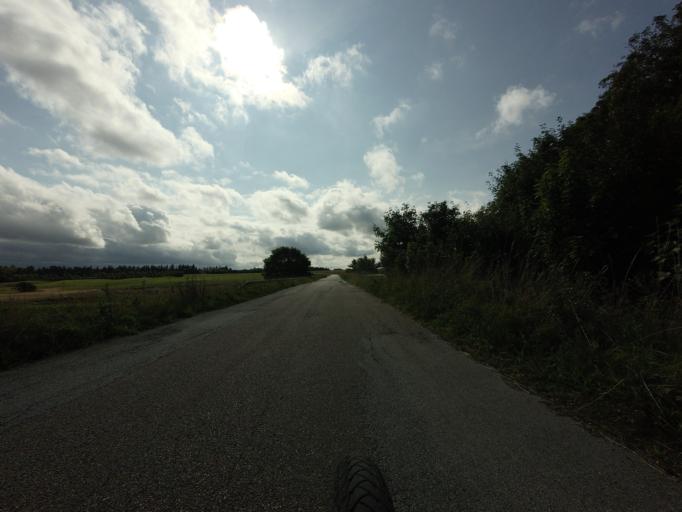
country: DK
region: North Denmark
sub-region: Hjorring Kommune
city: Hirtshals
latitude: 57.5509
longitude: 10.0599
